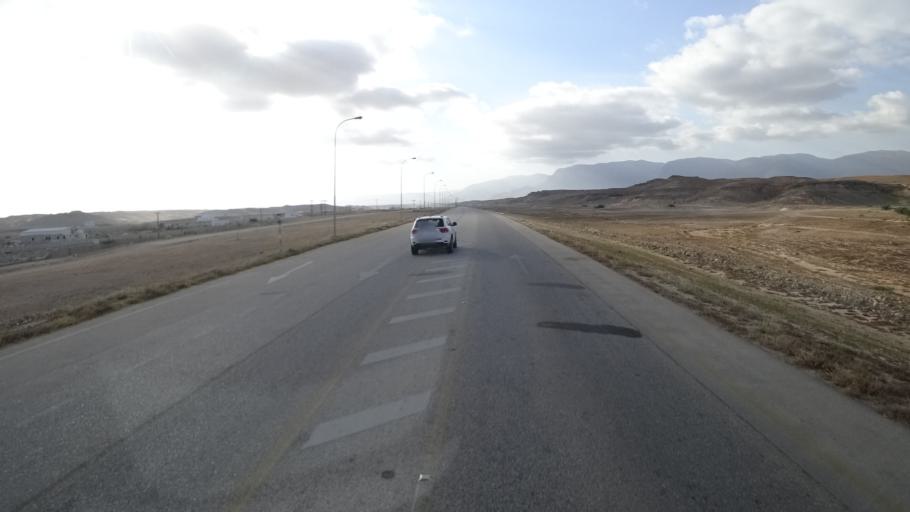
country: OM
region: Zufar
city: Salalah
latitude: 16.9561
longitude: 53.9116
